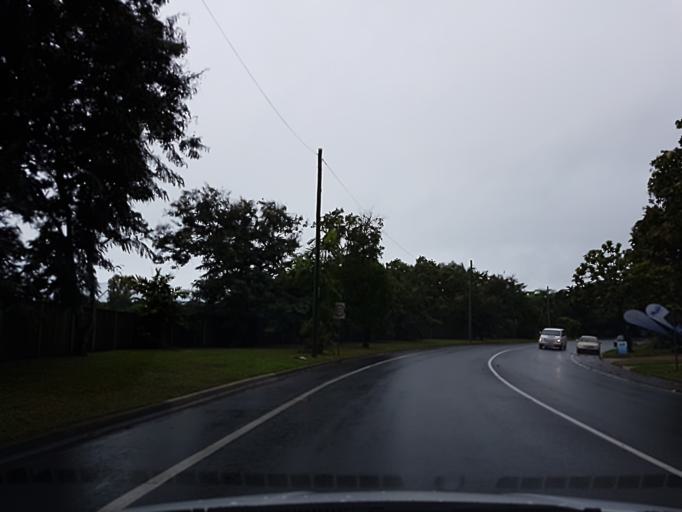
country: AU
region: Queensland
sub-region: Cairns
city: Palm Cove
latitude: -16.7451
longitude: 145.6637
